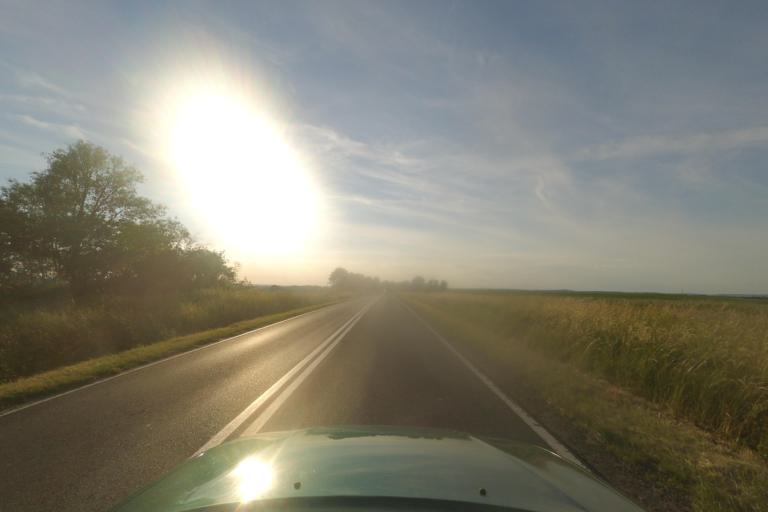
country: PL
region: Lower Silesian Voivodeship
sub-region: Powiat swidnicki
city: Swidnica
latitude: 50.8122
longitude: 16.5414
